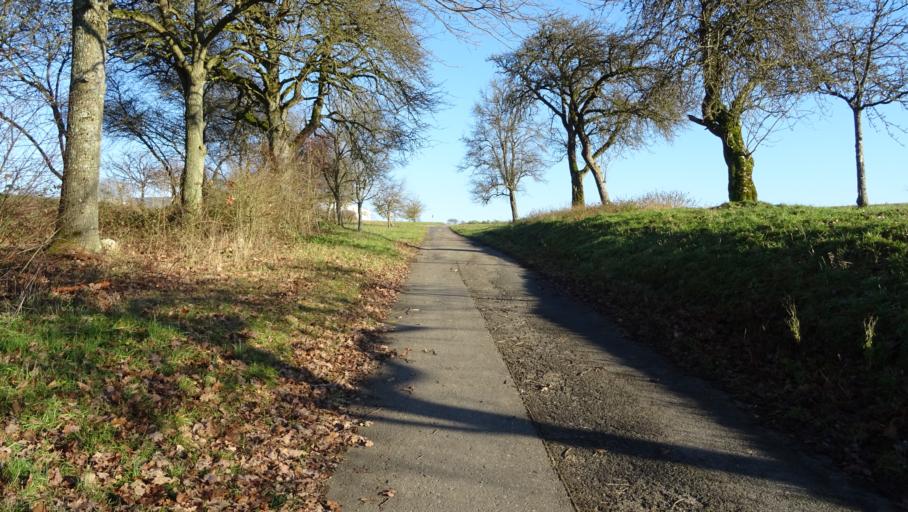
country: DE
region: Baden-Wuerttemberg
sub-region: Karlsruhe Region
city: Binau
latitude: 49.3443
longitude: 9.0421
